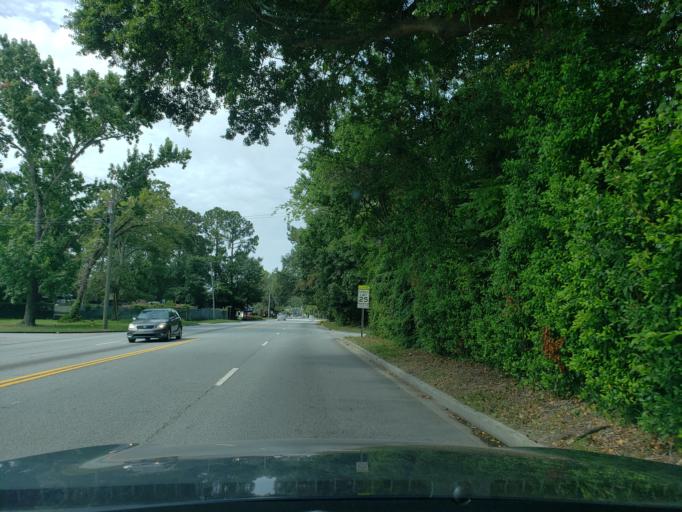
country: US
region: Georgia
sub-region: Chatham County
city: Thunderbolt
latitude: 32.0352
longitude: -81.0906
